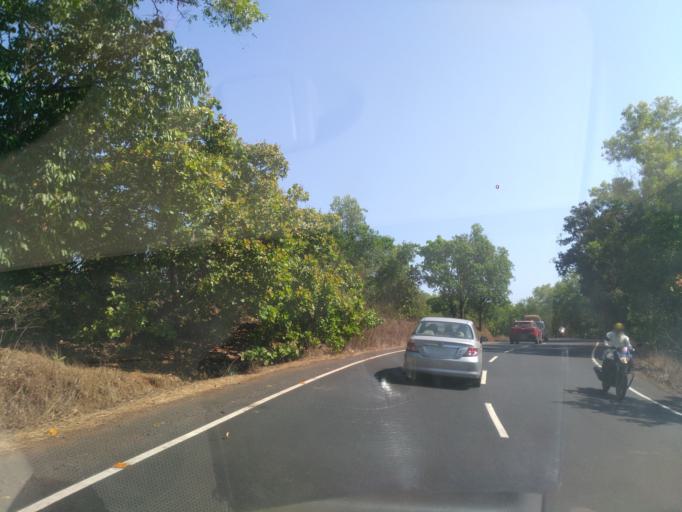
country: IN
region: Maharashtra
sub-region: Ratnagiri
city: Ratnagiri
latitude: 17.1233
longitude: 73.3830
